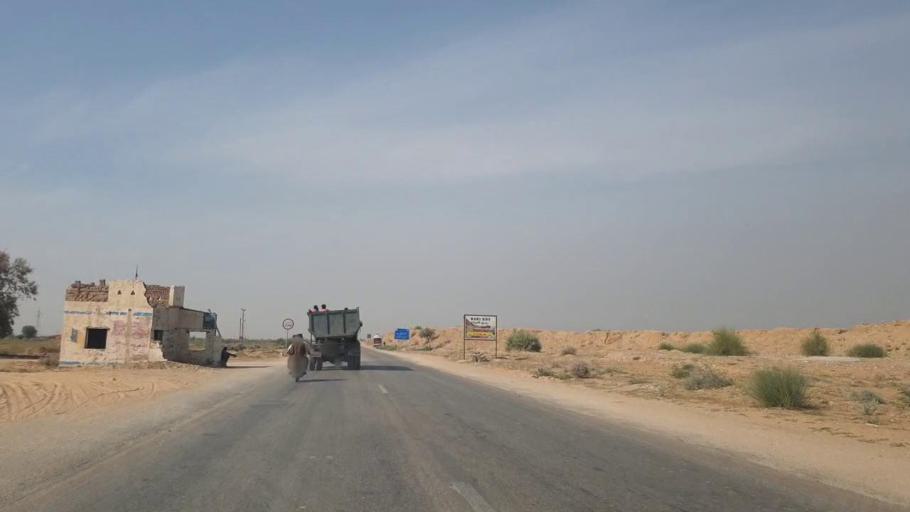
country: PK
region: Sindh
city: Sann
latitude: 26.0306
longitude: 68.1220
